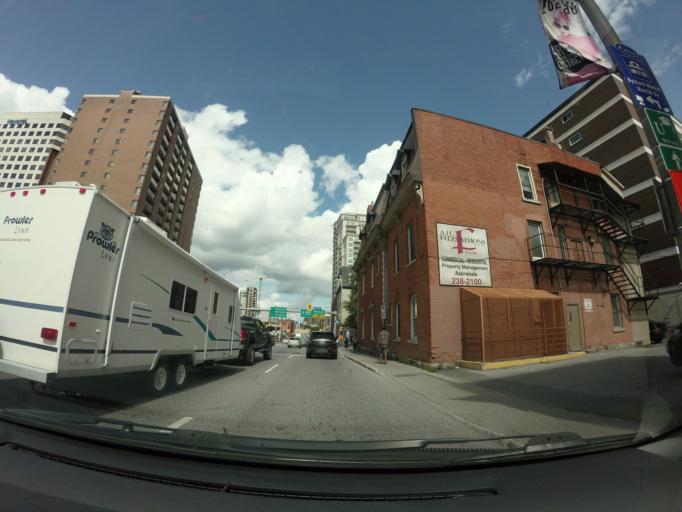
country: CA
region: Ontario
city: Ottawa
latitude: 45.4258
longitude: -75.6877
